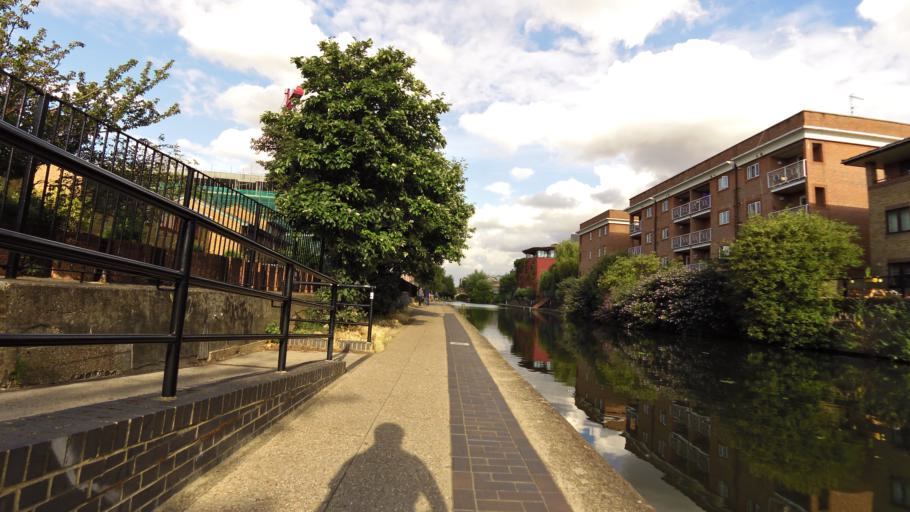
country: GB
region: England
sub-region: Greater London
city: Bethnal Green
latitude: 51.5363
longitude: -0.0747
